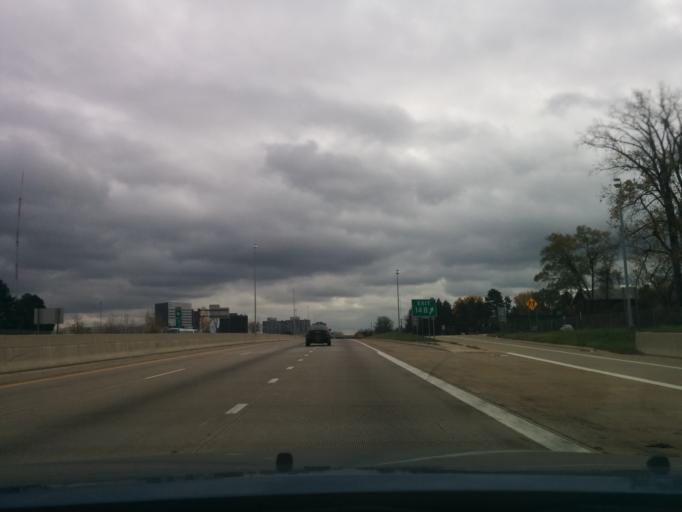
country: US
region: Michigan
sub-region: Oakland County
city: Southfield
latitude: 42.4635
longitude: -83.2285
